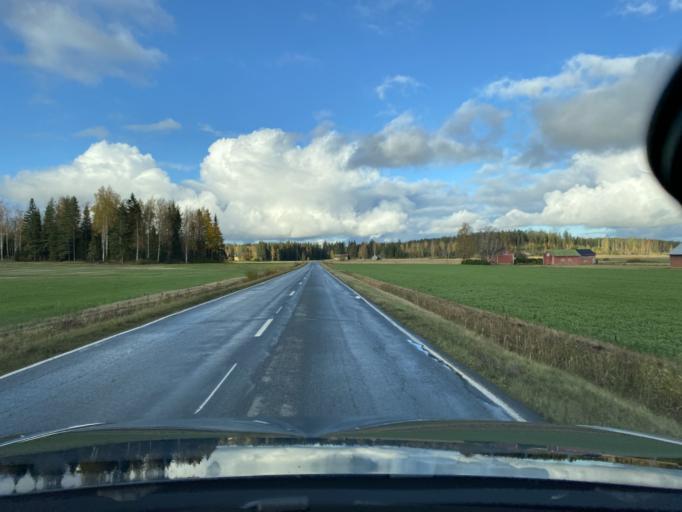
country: FI
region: Haeme
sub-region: Forssa
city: Humppila
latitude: 60.9831
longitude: 23.2534
